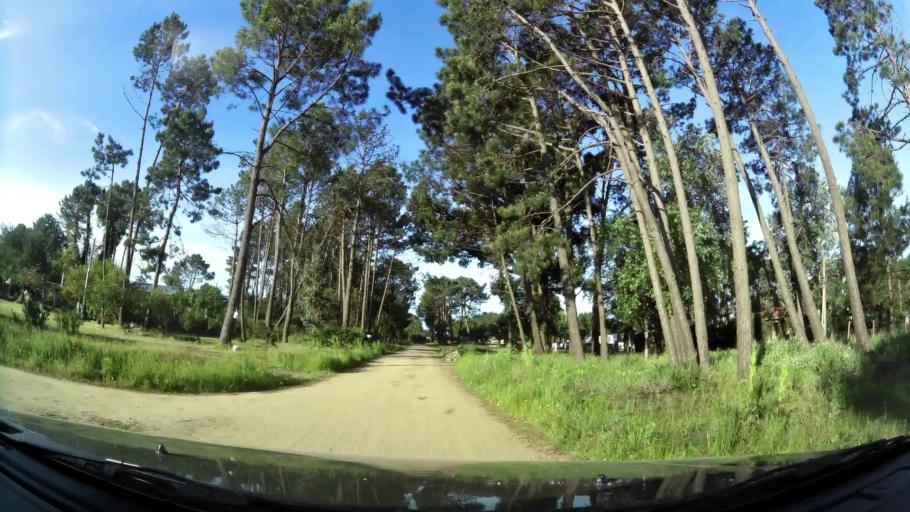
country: UY
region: Canelones
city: Empalme Olmos
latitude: -34.7695
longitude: -55.8567
